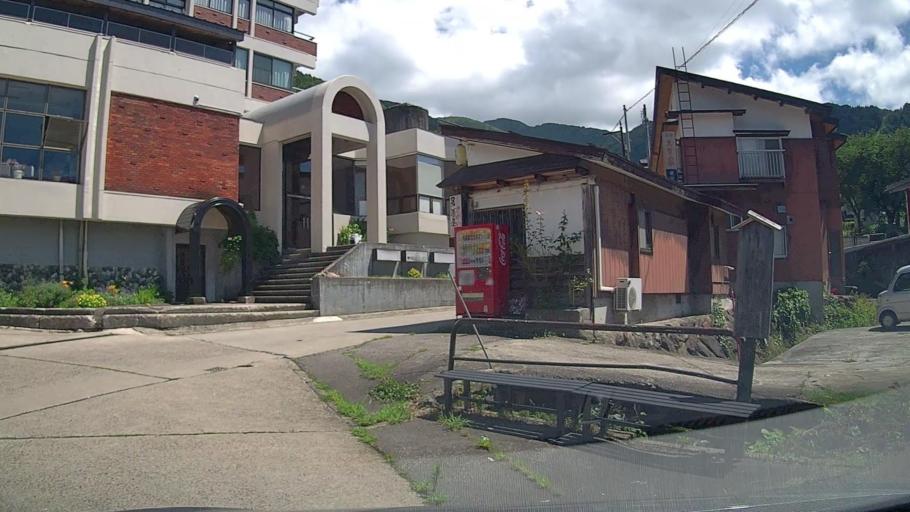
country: JP
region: Nagano
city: Iiyama
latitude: 36.9226
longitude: 138.4494
